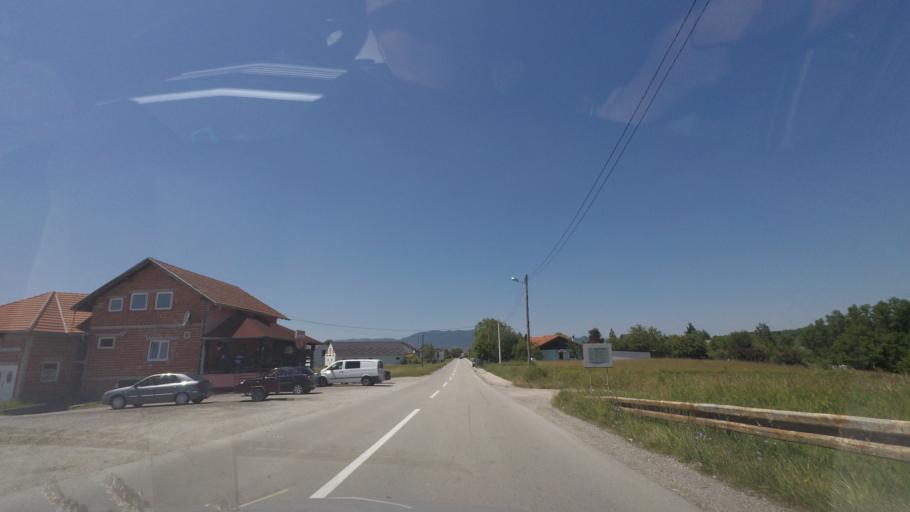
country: HR
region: Grad Zagreb
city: Horvati
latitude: 45.6769
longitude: 15.7574
